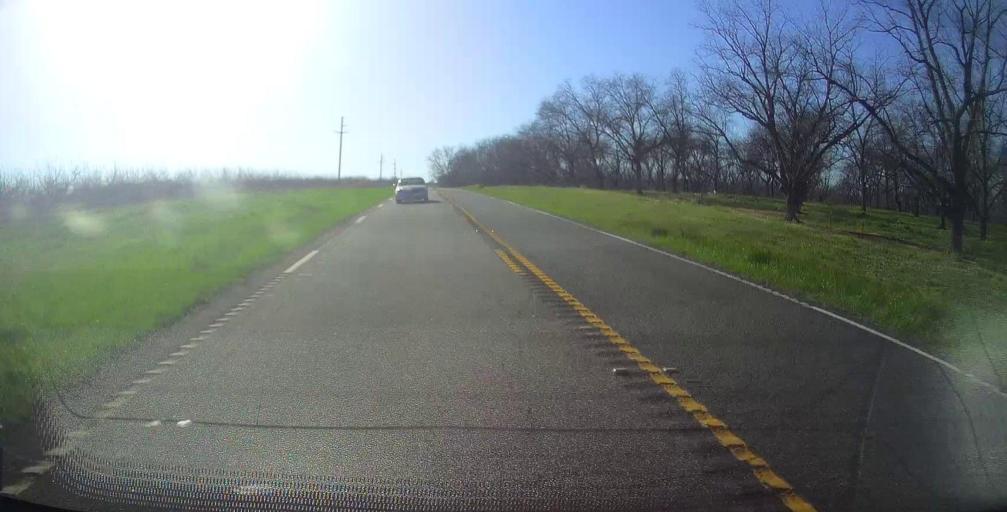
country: US
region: Georgia
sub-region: Macon County
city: Marshallville
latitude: 32.4394
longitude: -83.8608
